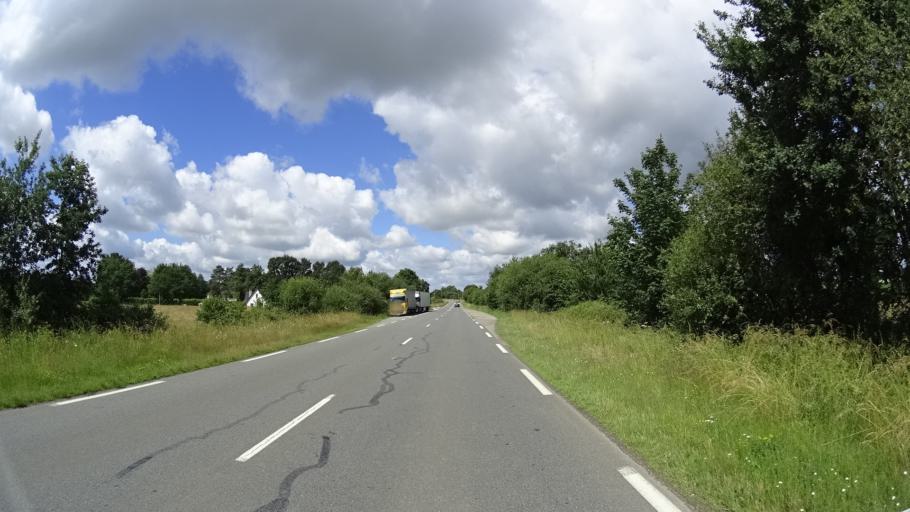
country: FR
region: Brittany
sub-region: Departement d'Ille-et-Vilaine
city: Le Rheu
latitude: 48.1168
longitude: -1.8153
